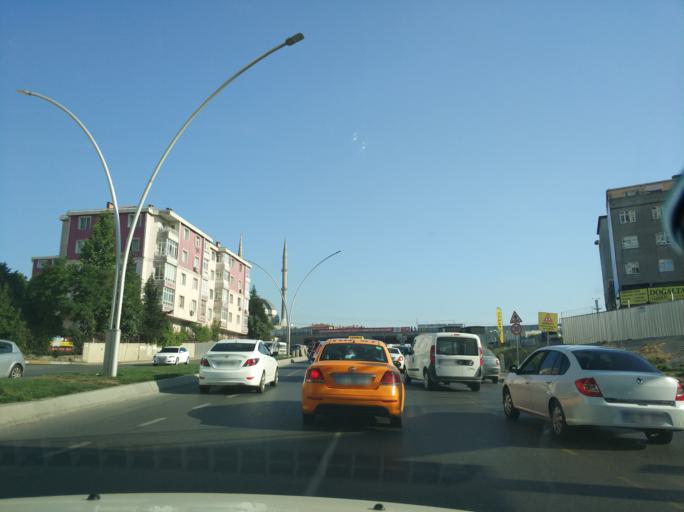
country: TR
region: Istanbul
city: Sultangazi
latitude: 41.0866
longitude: 28.9080
